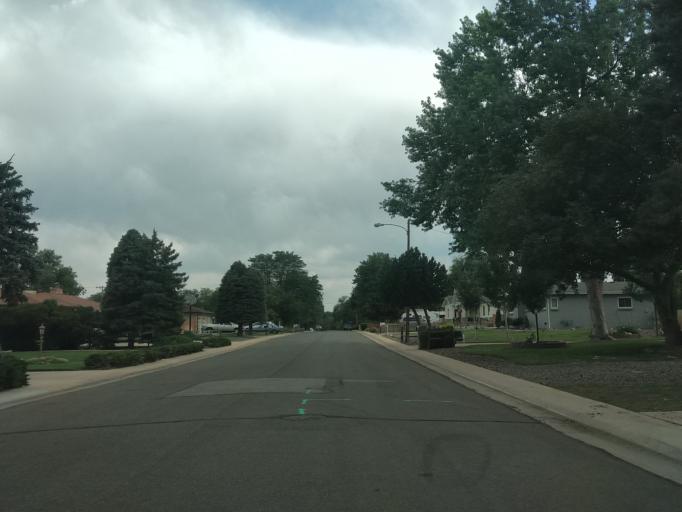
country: US
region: Colorado
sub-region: Jefferson County
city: Lakewood
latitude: 39.7027
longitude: -105.0991
